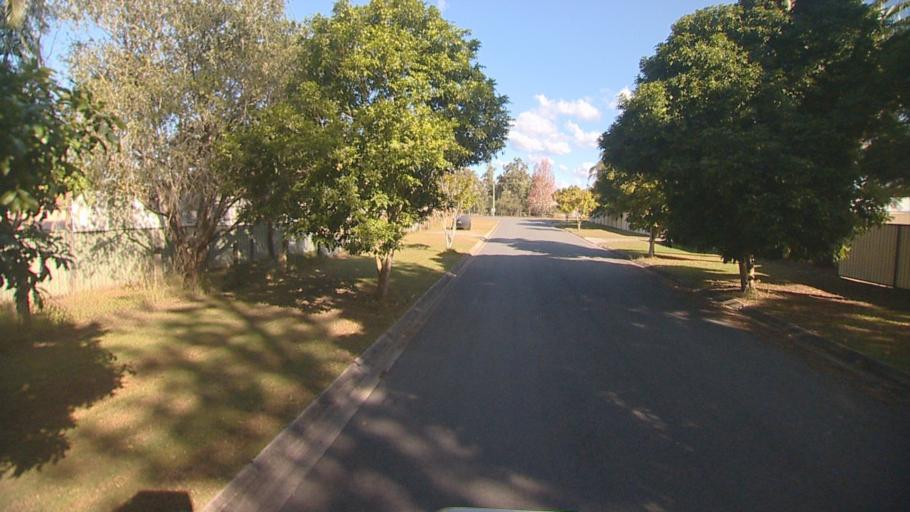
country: AU
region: Queensland
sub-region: Logan
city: Park Ridge South
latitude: -27.7078
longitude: 153.0149
